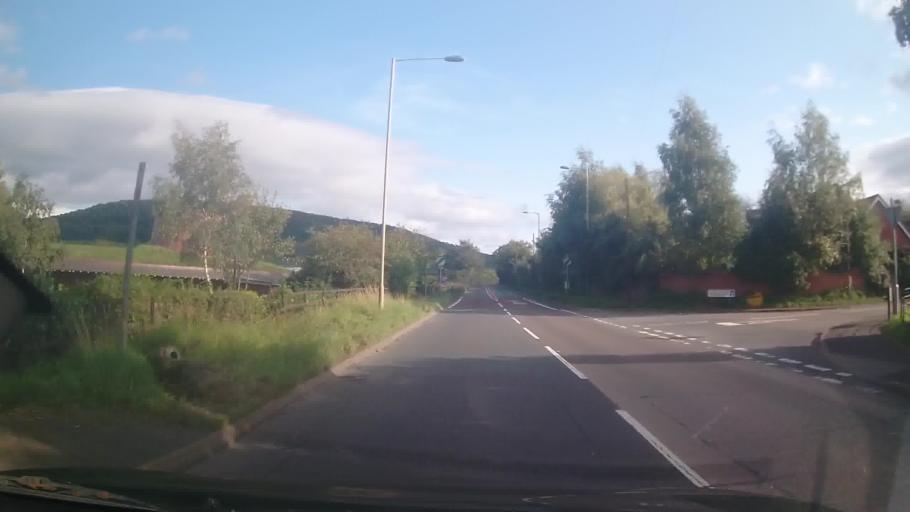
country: GB
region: England
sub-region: Shropshire
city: Craven Arms
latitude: 52.4375
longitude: -2.8336
